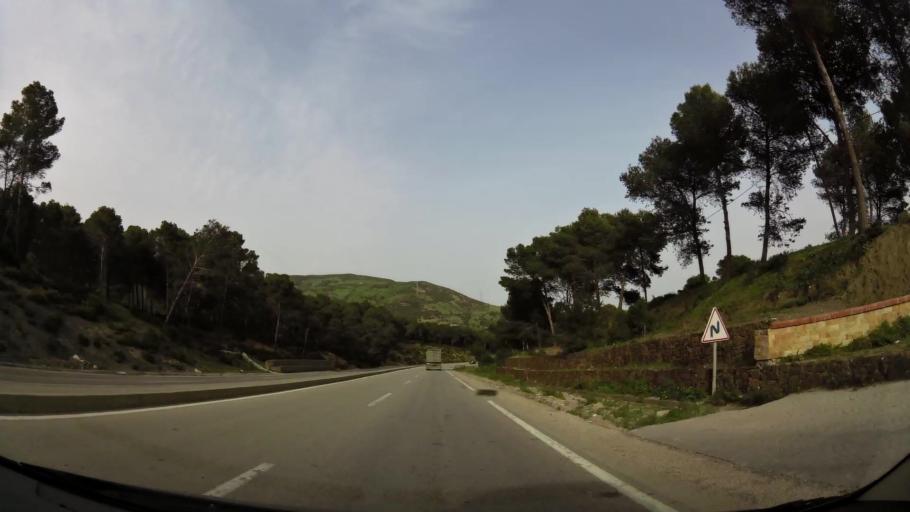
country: MA
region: Tanger-Tetouan
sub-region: Tetouan
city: Saddina
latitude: 35.5494
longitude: -5.5518
